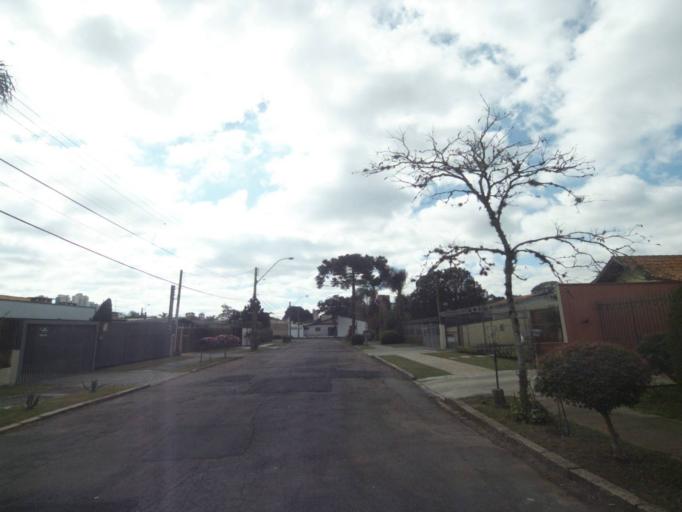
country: BR
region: Parana
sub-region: Curitiba
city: Curitiba
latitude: -25.4448
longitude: -49.3133
